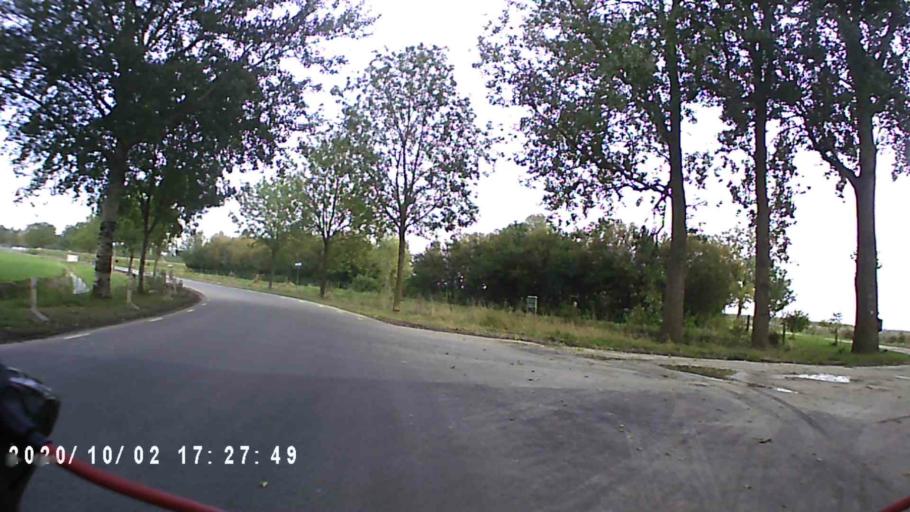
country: NL
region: Groningen
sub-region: Gemeente De Marne
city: Ulrum
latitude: 53.3360
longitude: 6.3136
